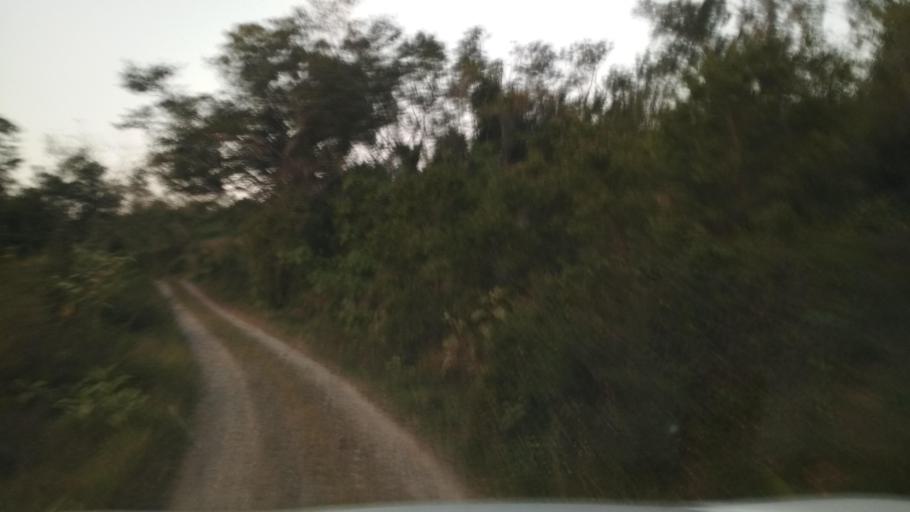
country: MX
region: Veracruz
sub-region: Poza Rica de Hidalgo
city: Arroyo del Maiz Uno
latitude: 20.4840
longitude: -97.3898
